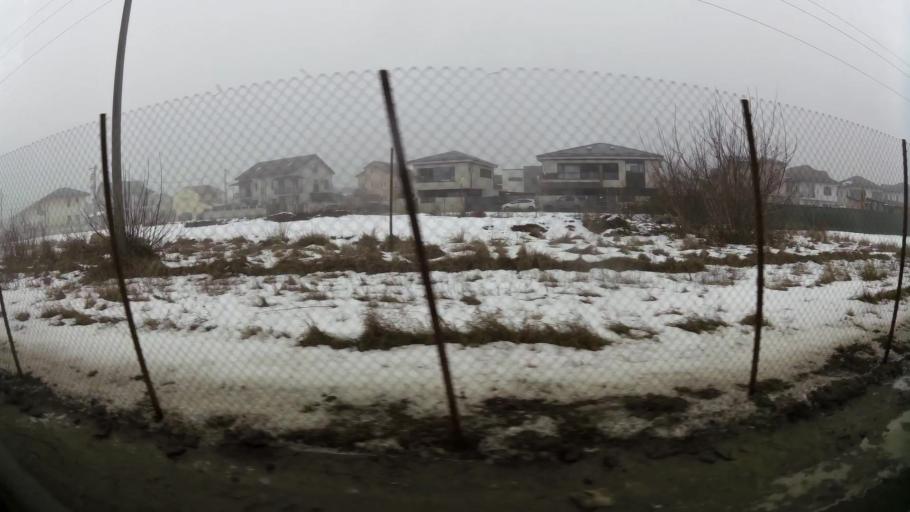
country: RO
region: Ilfov
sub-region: Comuna Chiajna
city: Chiajna
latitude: 44.4514
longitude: 25.9739
